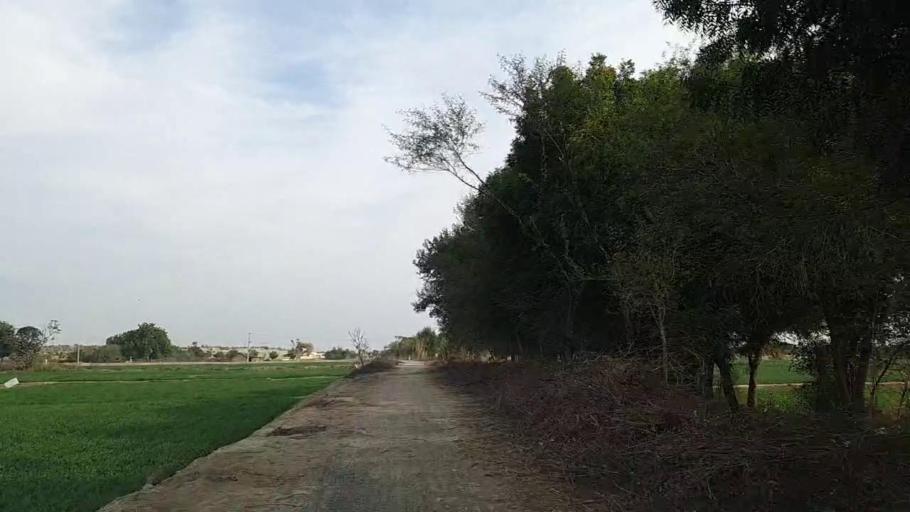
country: PK
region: Sindh
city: Jam Sahib
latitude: 26.4357
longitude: 68.6336
